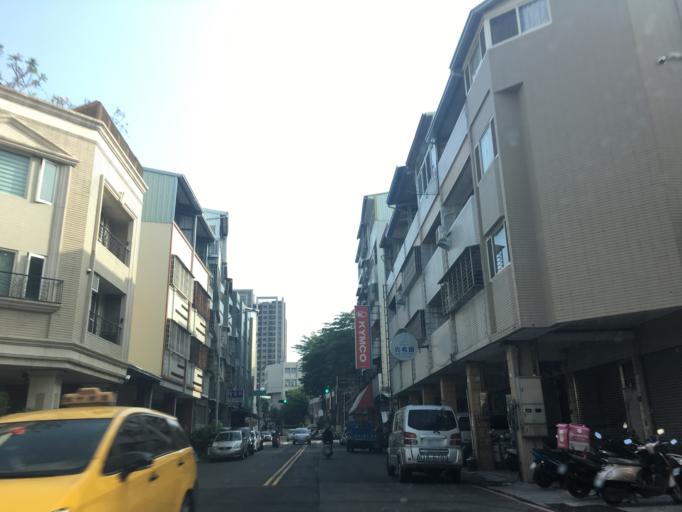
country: TW
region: Taiwan
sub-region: Taichung City
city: Taichung
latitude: 24.1690
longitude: 120.6803
